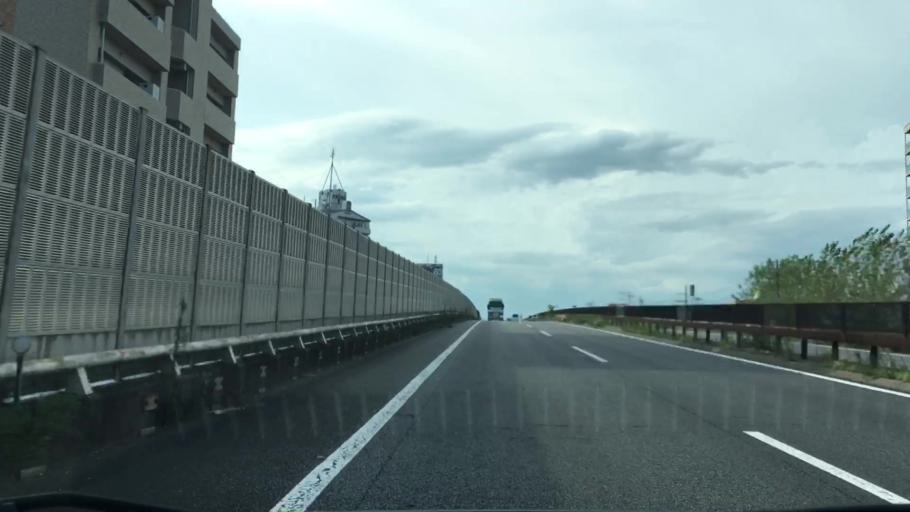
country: JP
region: Hyogo
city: Kakogawacho-honmachi
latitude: 34.7481
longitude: 134.8699
